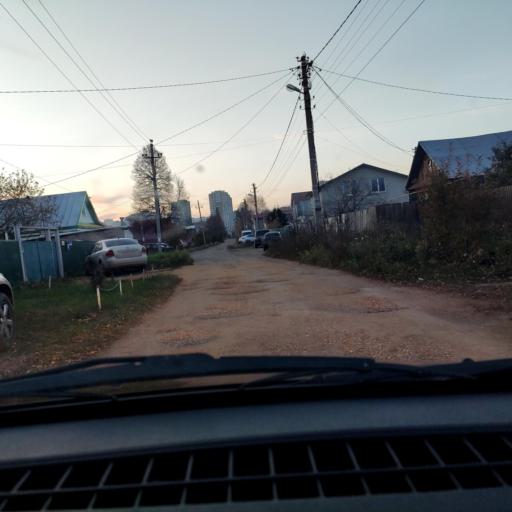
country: RU
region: Bashkortostan
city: Mikhaylovka
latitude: 54.7844
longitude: 55.8801
